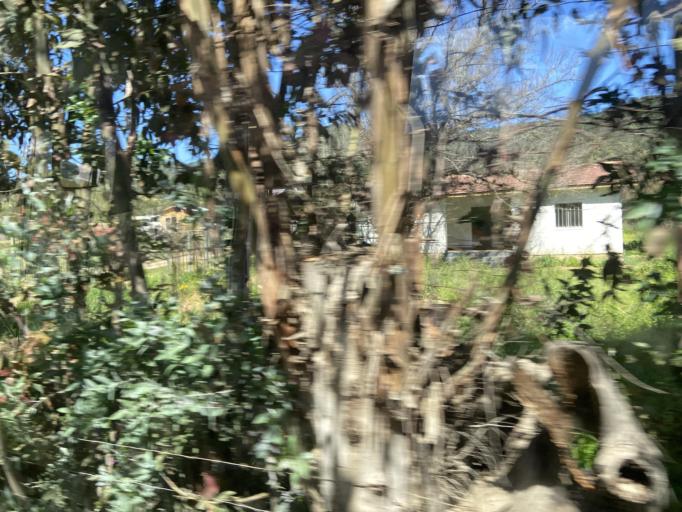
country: CL
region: Valparaiso
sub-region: Provincia de Marga Marga
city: Villa Alemana
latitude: -33.1635
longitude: -71.3198
